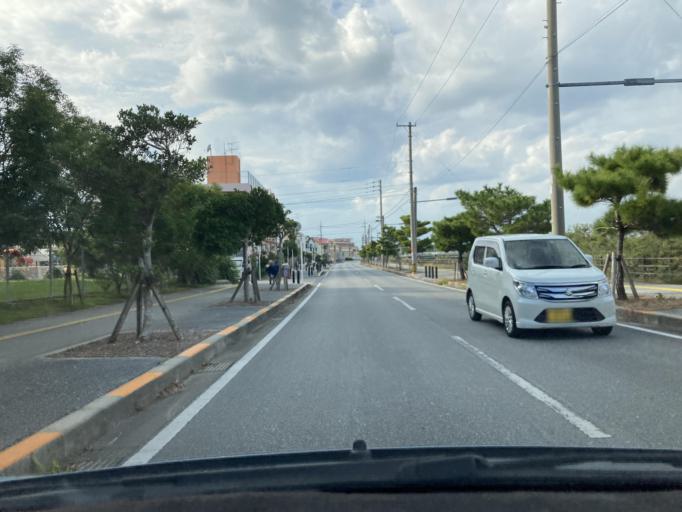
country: JP
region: Okinawa
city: Itoman
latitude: 26.1586
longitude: 127.6638
